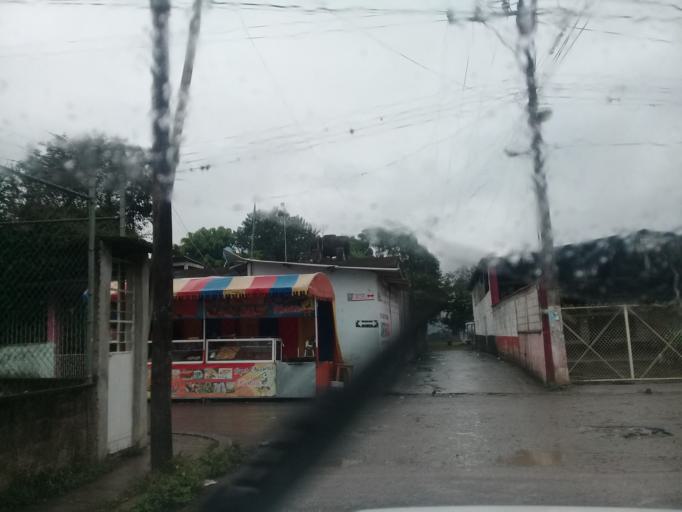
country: MX
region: Veracruz
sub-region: Cordoba
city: San Jose de Tapia
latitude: 18.8477
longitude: -96.9500
